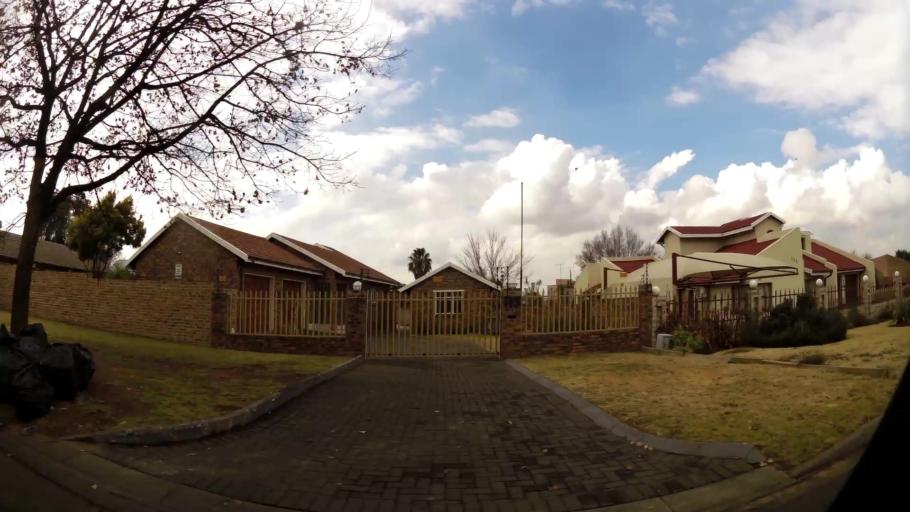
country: ZA
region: Gauteng
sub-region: Sedibeng District Municipality
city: Vanderbijlpark
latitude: -26.7335
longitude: 27.8543
